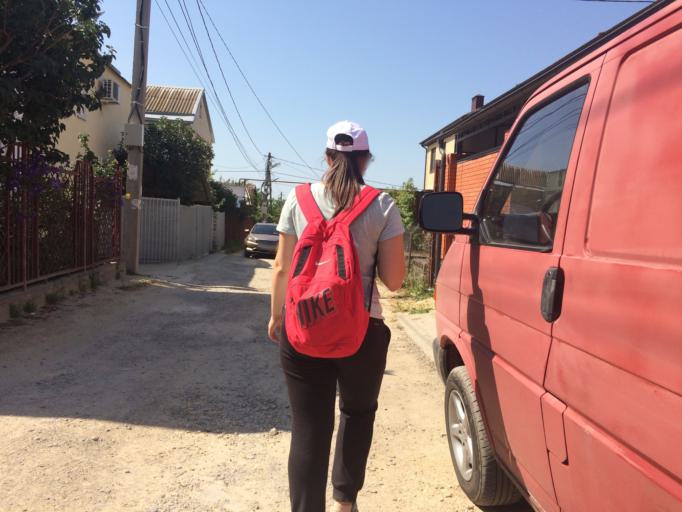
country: RU
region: Stavropol'skiy
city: Tatarka
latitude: 44.9852
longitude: 41.9419
